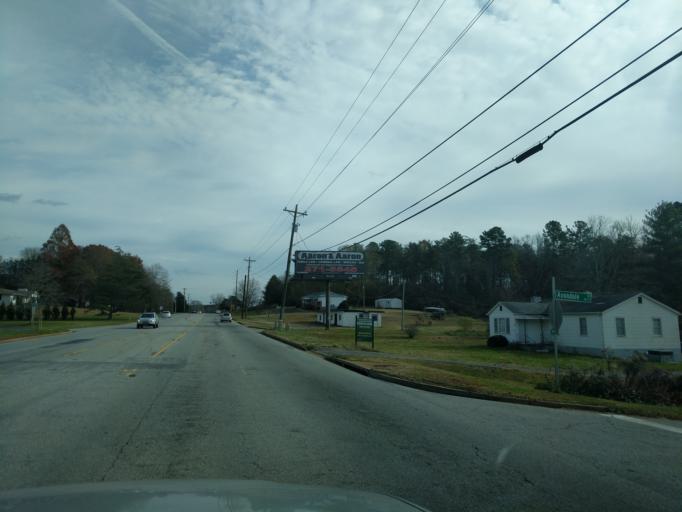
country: US
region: South Carolina
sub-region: Oconee County
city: Walhalla
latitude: 34.7206
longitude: -83.0123
